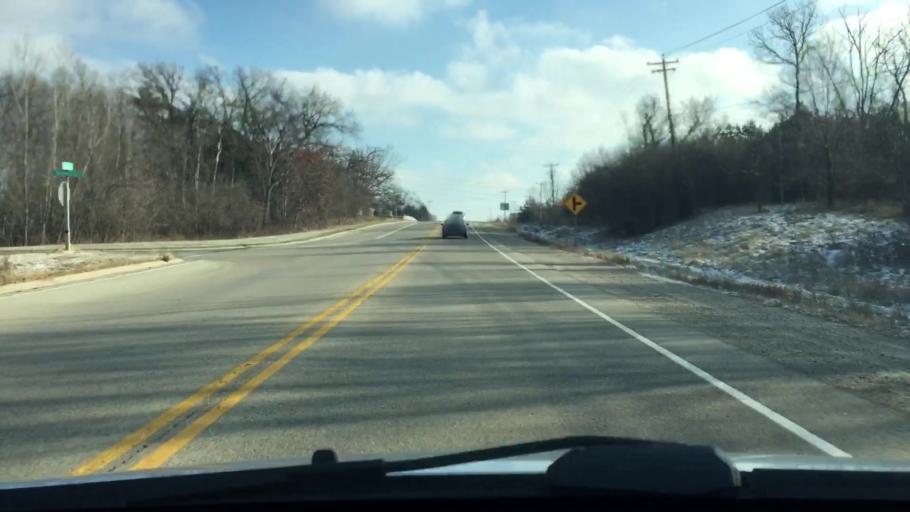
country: US
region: Wisconsin
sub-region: Waukesha County
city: Dousman
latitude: 43.0182
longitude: -88.4268
